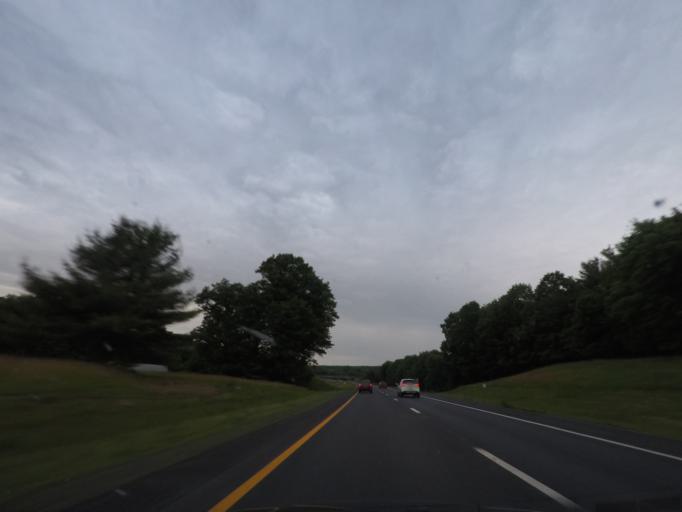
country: US
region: New York
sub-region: Rensselaer County
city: Nassau
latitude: 42.4553
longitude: -73.5779
